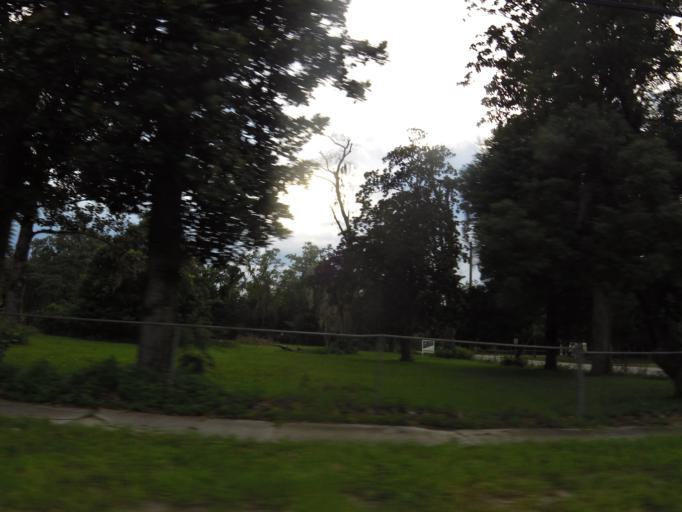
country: US
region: Florida
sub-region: Duval County
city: Jacksonville
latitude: 30.3134
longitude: -81.7836
